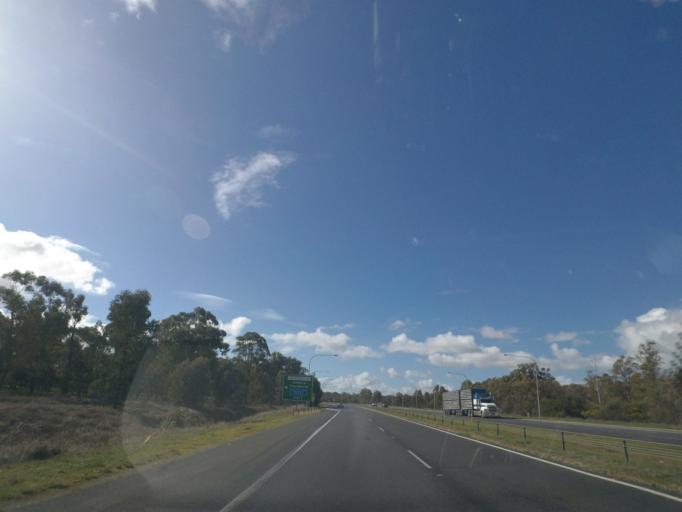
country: AU
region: New South Wales
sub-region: Albury Municipality
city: Lavington
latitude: -36.0444
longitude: 146.9692
